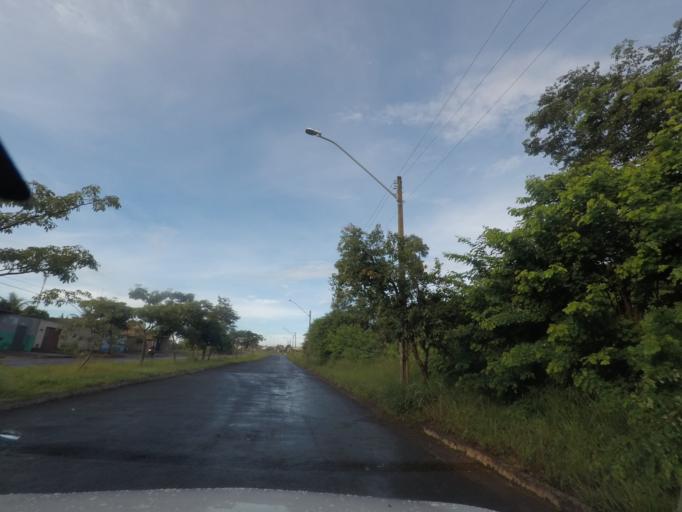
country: BR
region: Goias
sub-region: Goiania
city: Goiania
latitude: -16.7499
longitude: -49.3761
